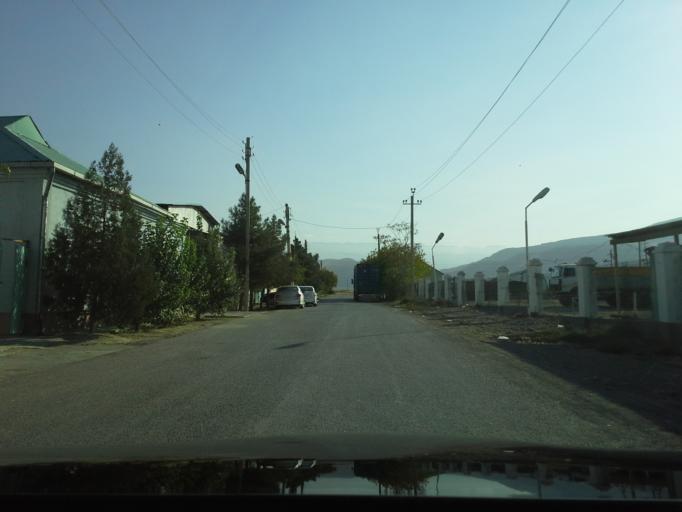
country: TM
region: Ahal
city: Abadan
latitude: 38.0516
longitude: 58.1629
